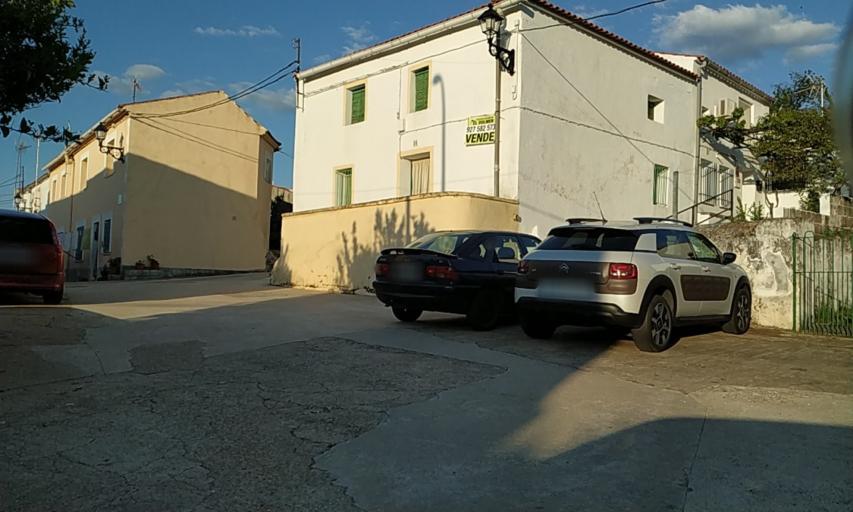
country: PT
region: Portalegre
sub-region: Portalegre
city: Sao Juliao
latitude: 39.3490
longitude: -7.2752
